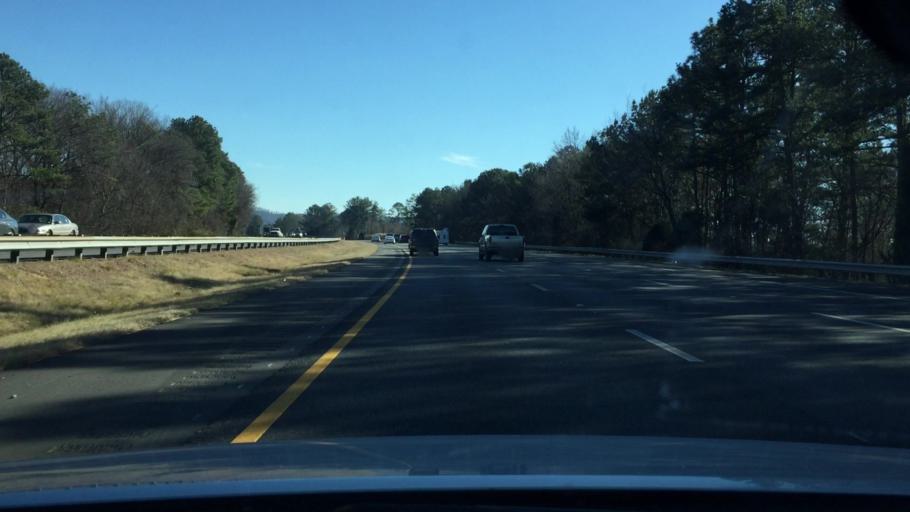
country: US
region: Georgia
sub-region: Catoosa County
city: Ringgold
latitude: 34.9165
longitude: -85.1454
